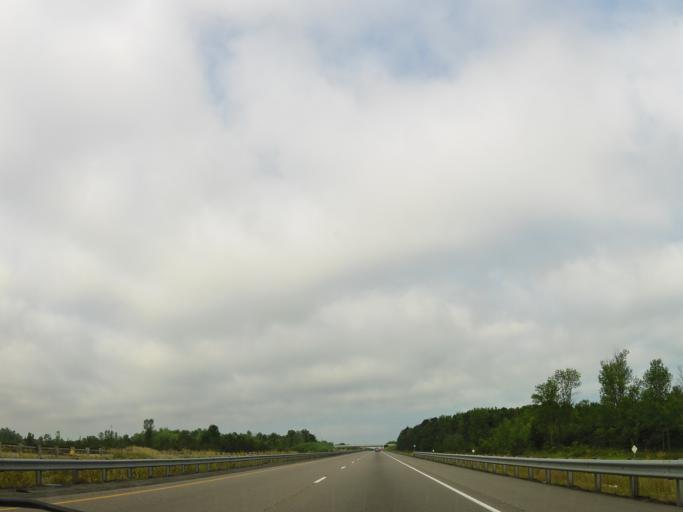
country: CA
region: Ontario
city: Skatepark
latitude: 44.2755
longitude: -76.8709
